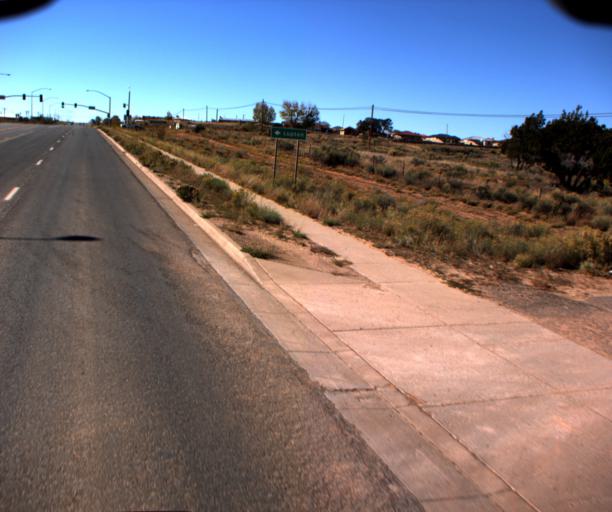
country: US
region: Arizona
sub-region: Apache County
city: Saint Michaels
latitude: 35.6577
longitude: -109.0873
